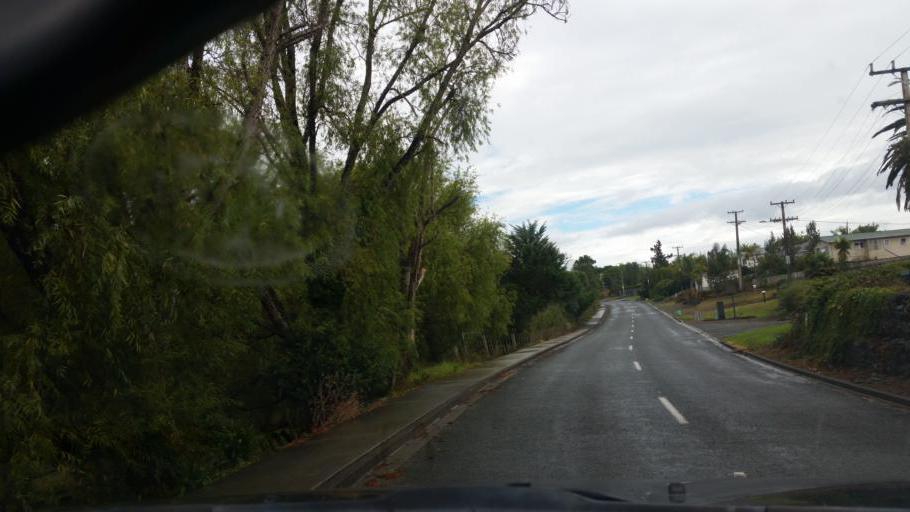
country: NZ
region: Northland
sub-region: Whangarei
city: Ruakaka
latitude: -36.1098
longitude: 174.3623
